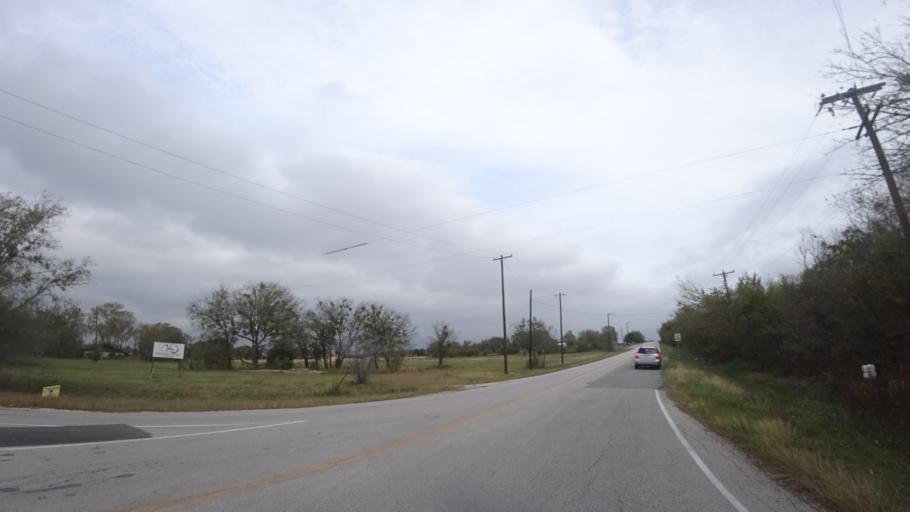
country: US
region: Texas
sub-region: Travis County
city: Pflugerville
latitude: 30.3955
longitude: -97.5897
